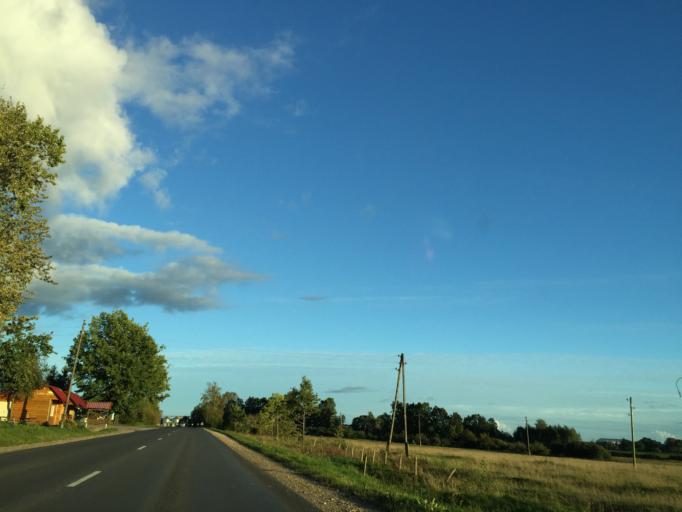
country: LV
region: Saldus Rajons
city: Saldus
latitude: 56.6916
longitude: 22.4488
